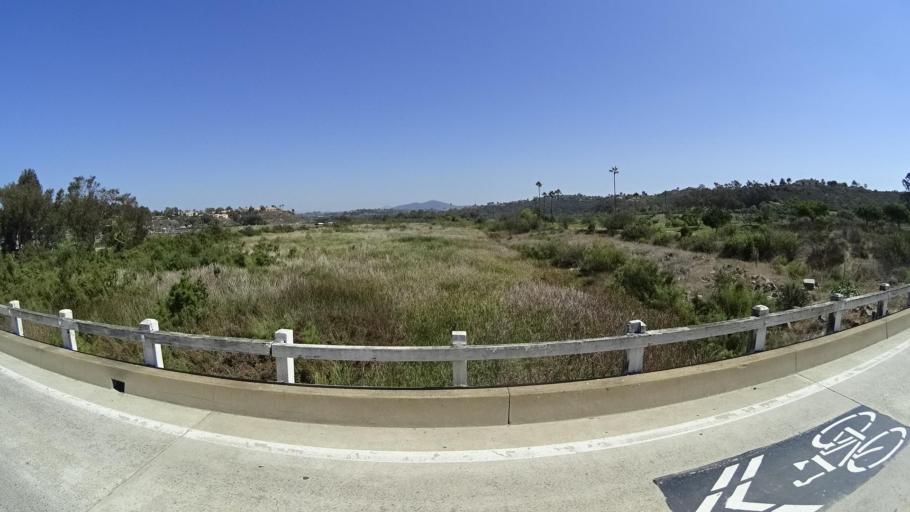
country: US
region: California
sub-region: San Diego County
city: Del Mar
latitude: 32.9778
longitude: -117.2304
